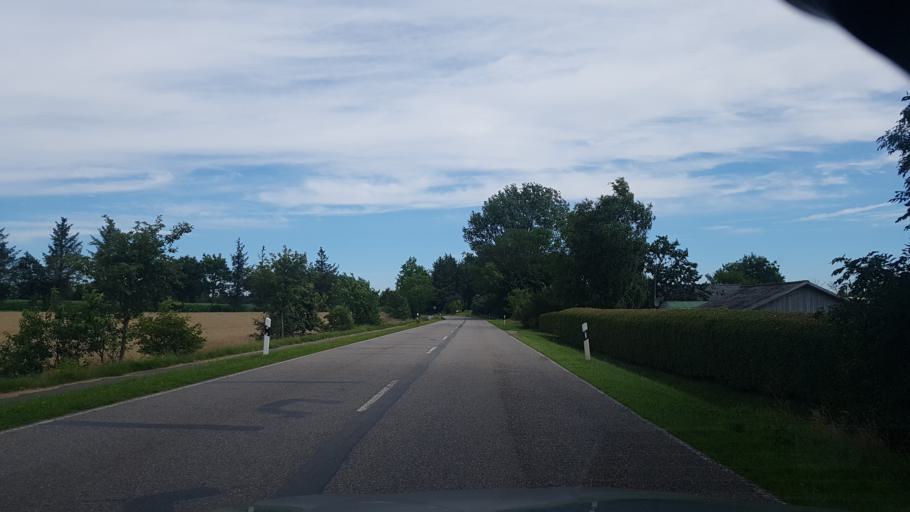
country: DE
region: Schleswig-Holstein
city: Ladelund
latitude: 54.8454
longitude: 9.0352
